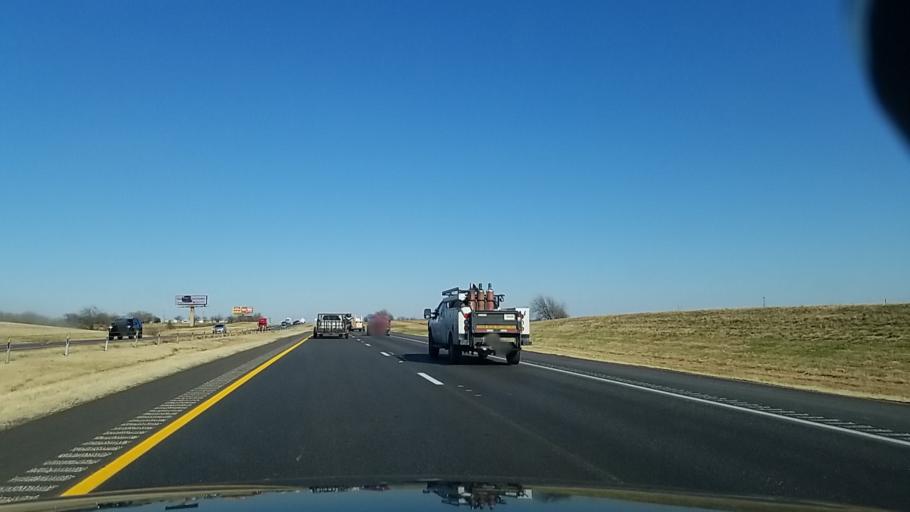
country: US
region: Texas
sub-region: Denton County
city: Northlake
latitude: 33.0914
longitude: -97.2291
